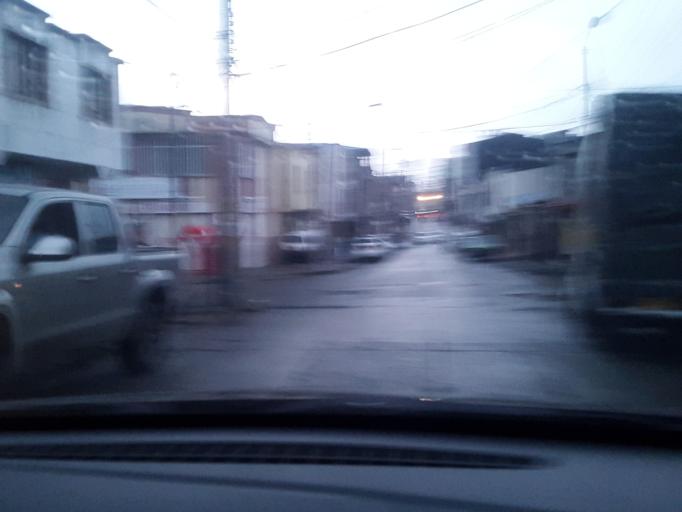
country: CO
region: Quindio
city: Armenia
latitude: 4.5397
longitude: -75.6742
